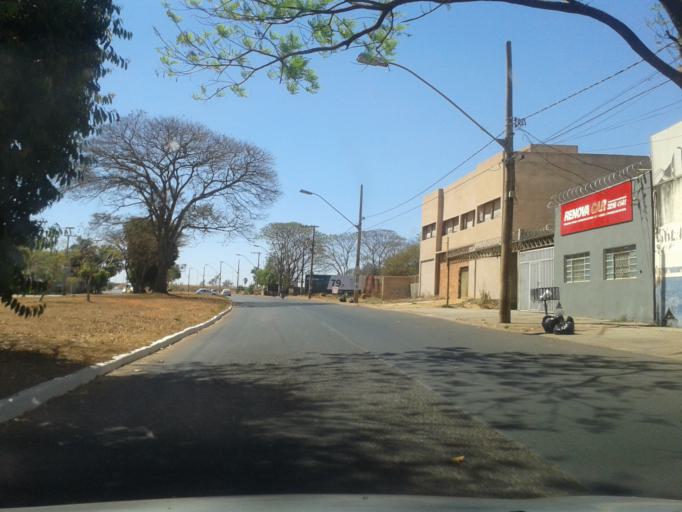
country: BR
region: Minas Gerais
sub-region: Uberlandia
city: Uberlandia
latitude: -18.9391
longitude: -48.2256
